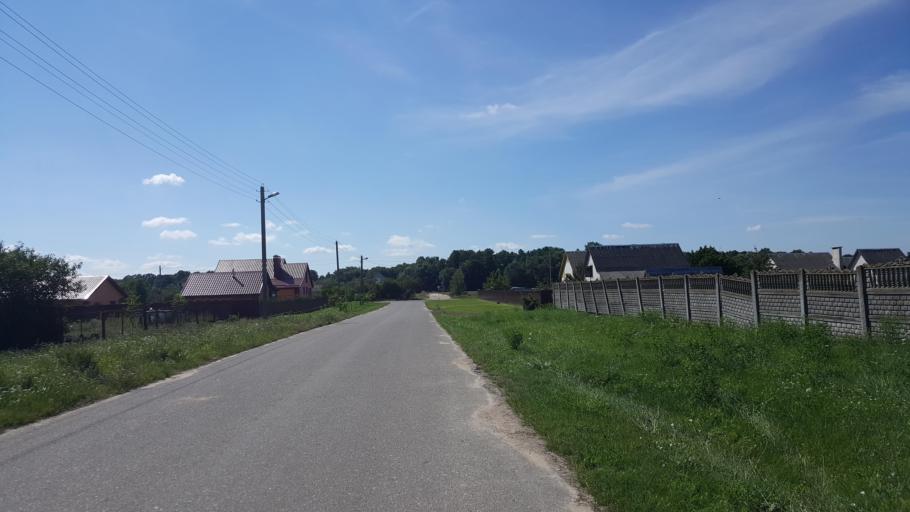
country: BY
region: Brest
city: Charnawchytsy
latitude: 52.2744
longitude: 23.7583
